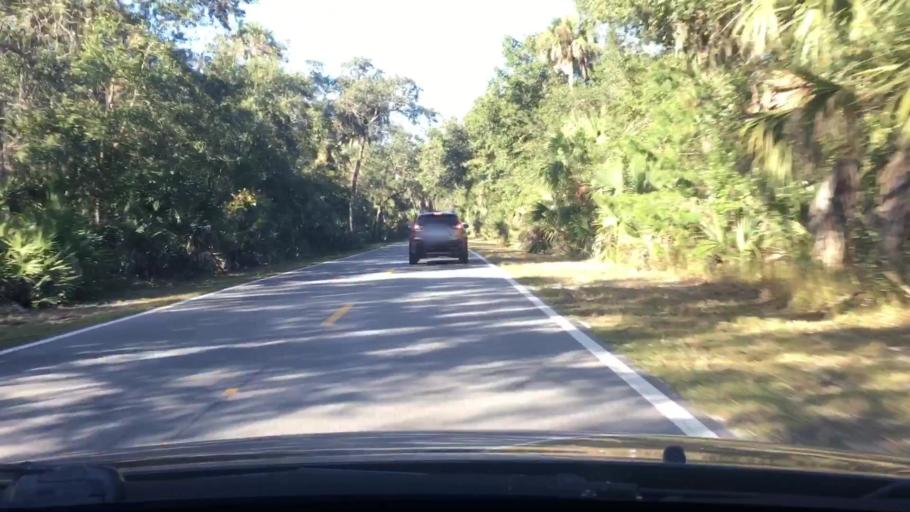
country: US
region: Florida
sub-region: Volusia County
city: Ormond-by-the-Sea
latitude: 29.3836
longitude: -81.1309
